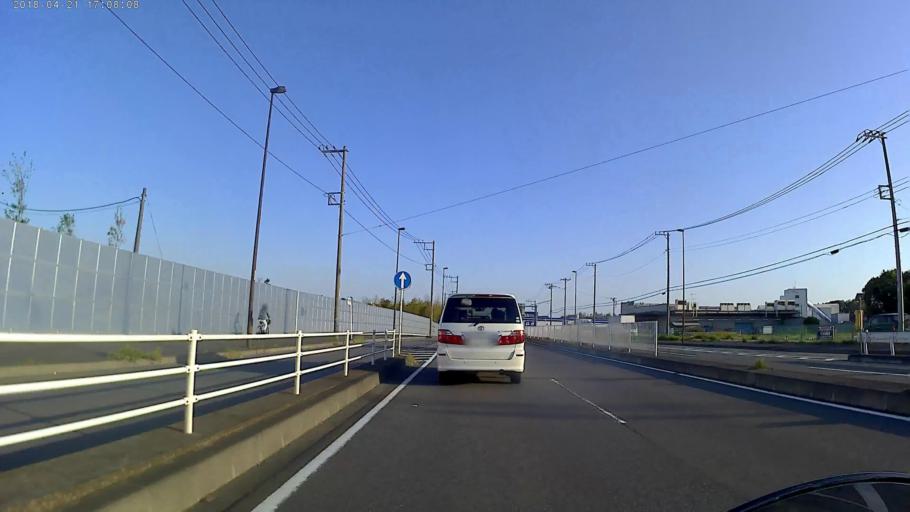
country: JP
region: Kanagawa
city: Fujisawa
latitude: 35.4053
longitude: 139.4409
